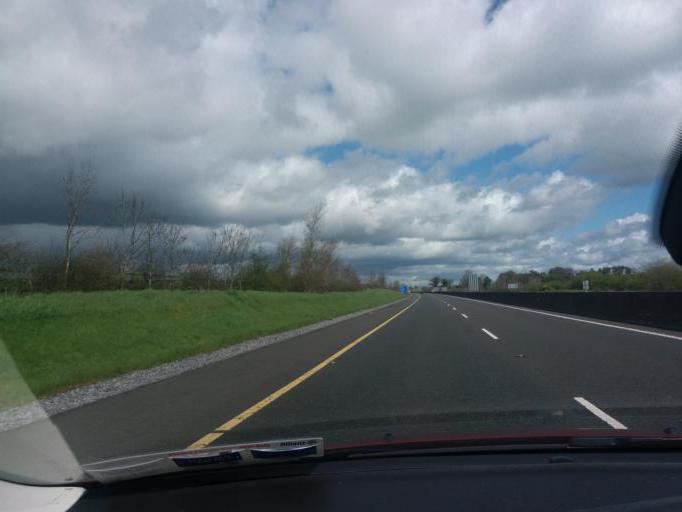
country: IE
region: Leinster
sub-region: Laois
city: Rathdowney
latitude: 52.7371
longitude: -7.5789
